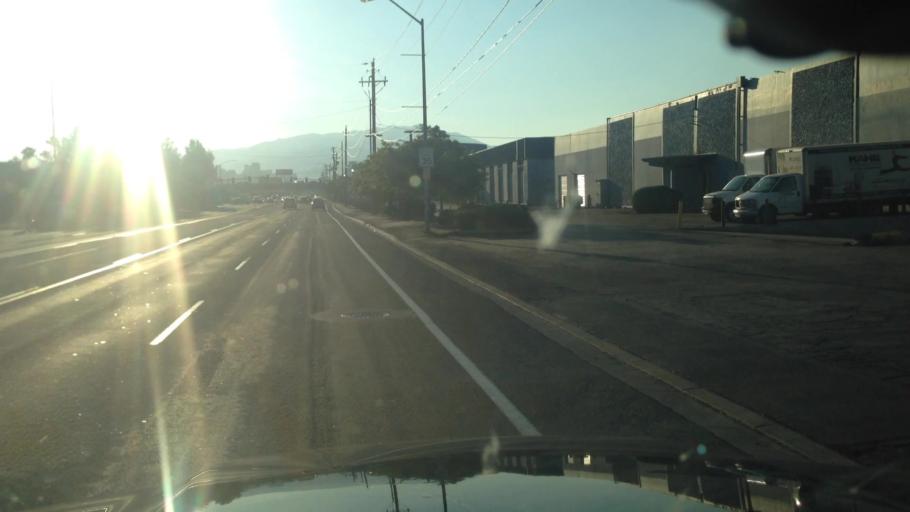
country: US
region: Nevada
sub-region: Washoe County
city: Sparks
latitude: 39.5180
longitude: -119.7784
